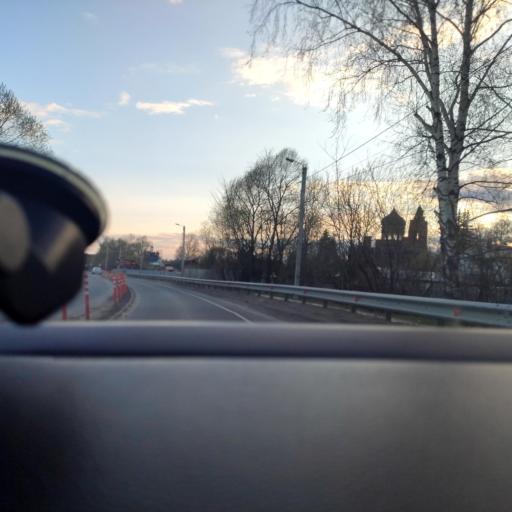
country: RU
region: Moskovskaya
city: Krasnyy Tkach
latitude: 55.4280
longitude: 39.1958
